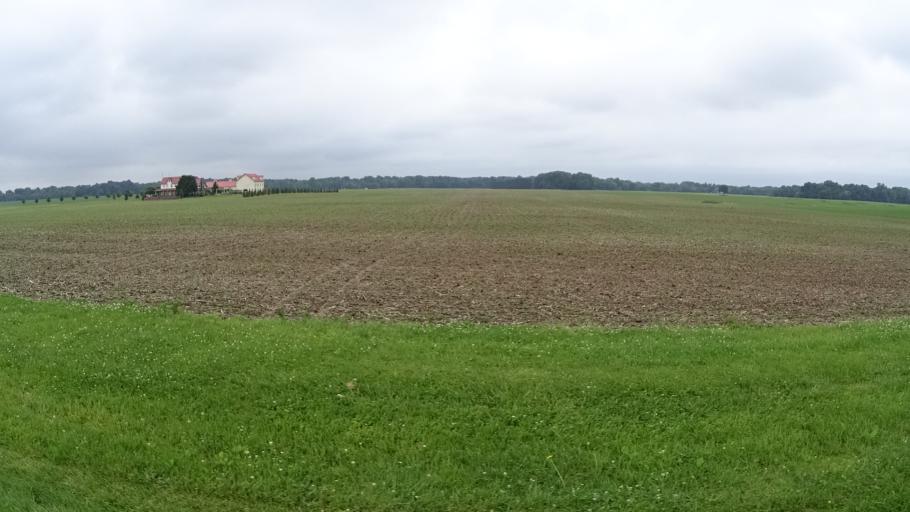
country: US
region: Ohio
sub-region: Erie County
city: Milan
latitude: 41.3153
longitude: -82.5433
